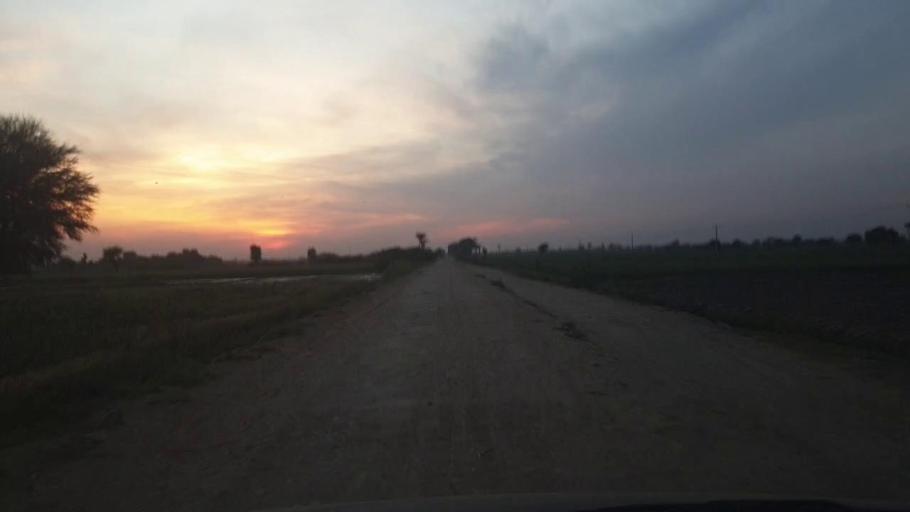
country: PK
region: Sindh
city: Kunri
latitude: 25.2240
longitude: 69.5331
